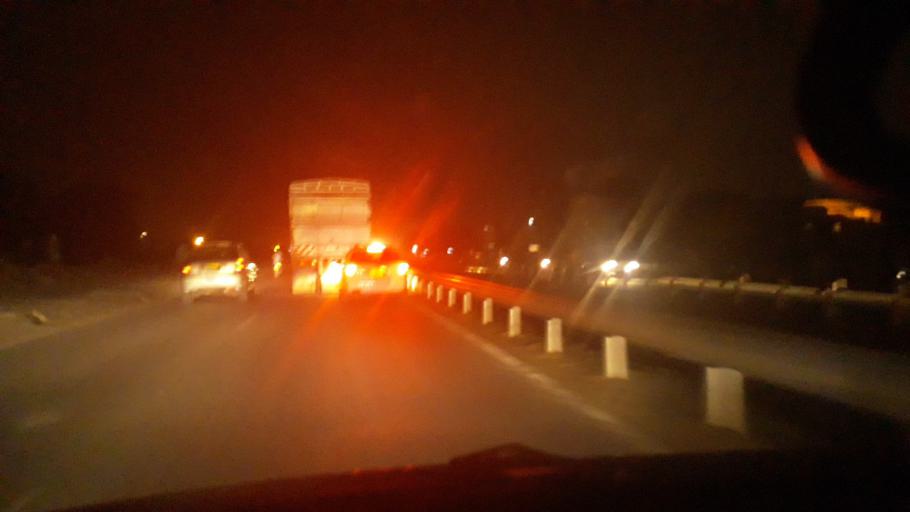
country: KE
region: Nairobi Area
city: Pumwani
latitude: -1.2843
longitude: 36.8836
